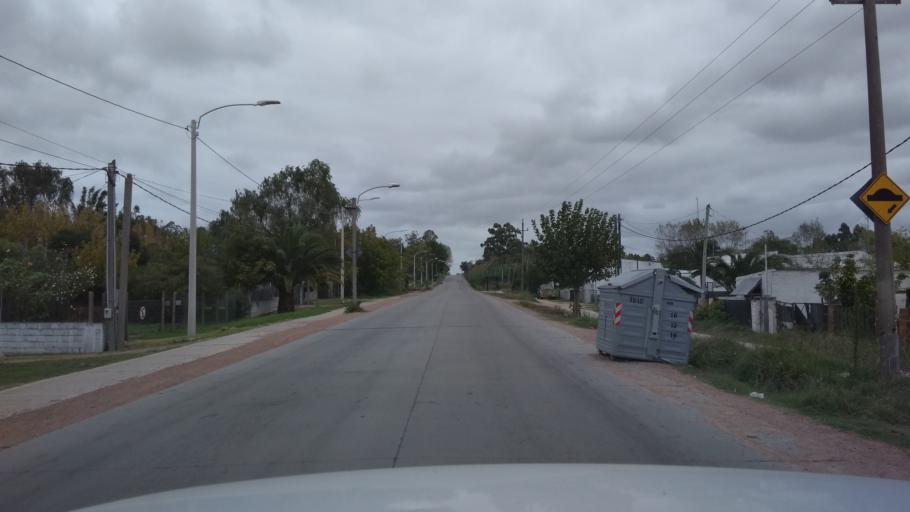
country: UY
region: Canelones
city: Toledo
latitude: -34.7840
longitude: -56.1393
